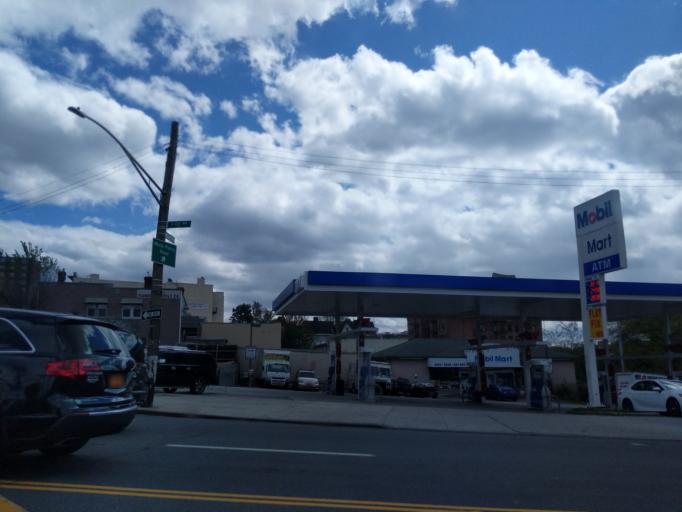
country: US
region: New York
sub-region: Bronx
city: The Bronx
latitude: 40.8777
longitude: -73.8675
